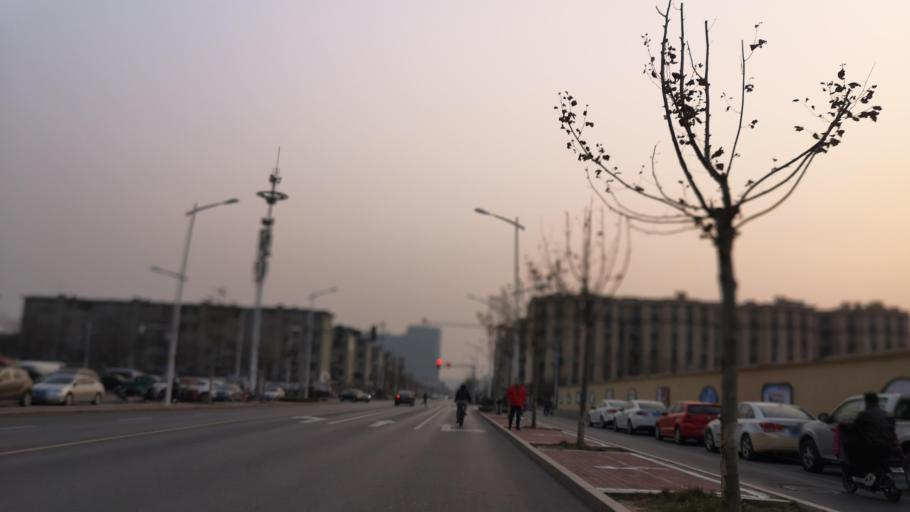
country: CN
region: Henan Sheng
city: Zhongyuanlu
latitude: 35.7844
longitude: 115.0812
